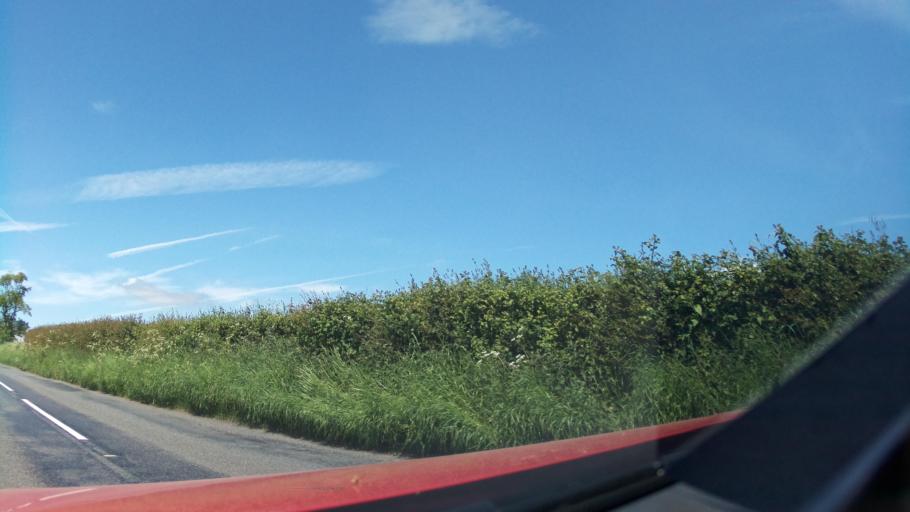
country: GB
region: Wales
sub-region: Monmouthshire
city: Caldicot
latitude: 51.6319
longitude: -2.7439
